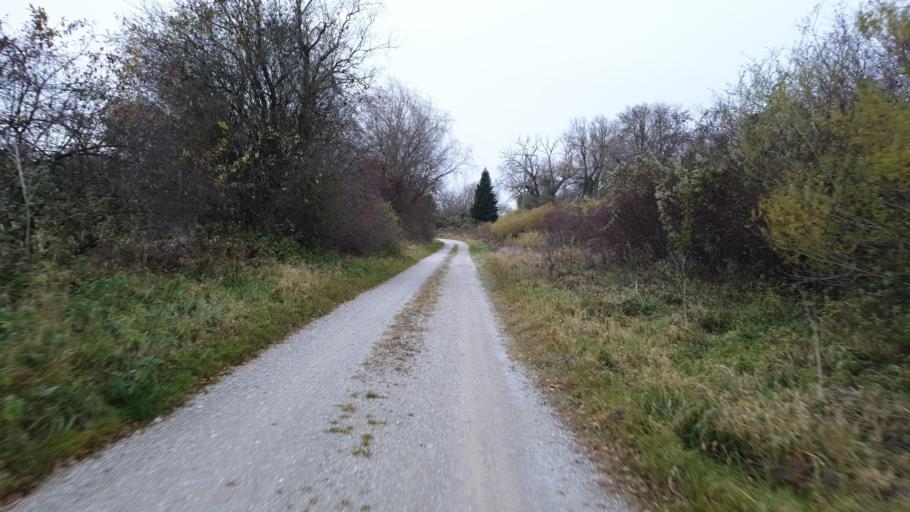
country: DE
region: Bavaria
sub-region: Upper Bavaria
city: Aschheim
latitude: 48.2043
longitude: 11.7039
